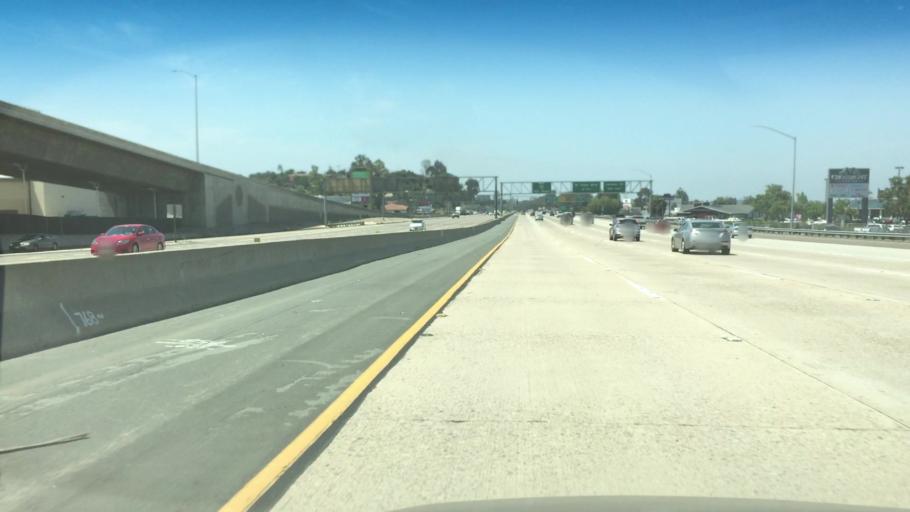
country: US
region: California
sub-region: San Diego County
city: La Mesa
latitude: 32.7764
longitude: -117.0071
